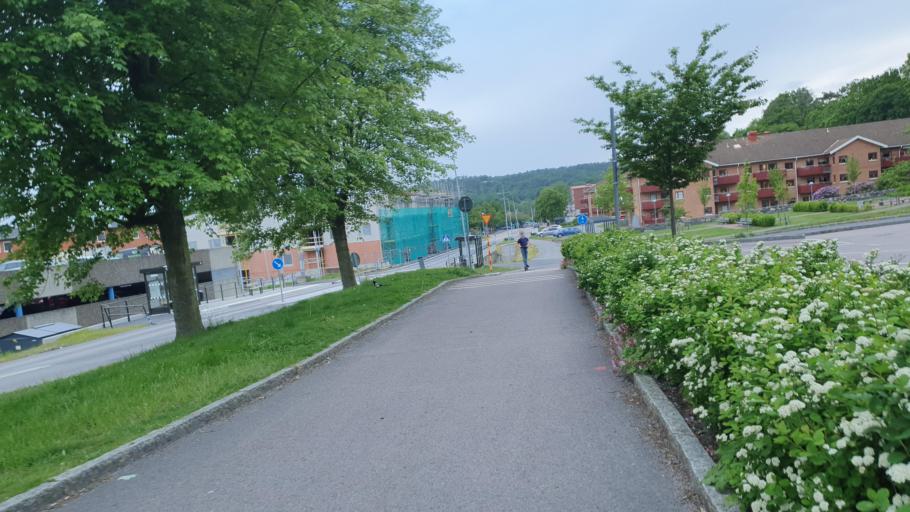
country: SE
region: Vaestra Goetaland
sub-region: Molndal
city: Kallered
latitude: 57.6107
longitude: 12.0549
